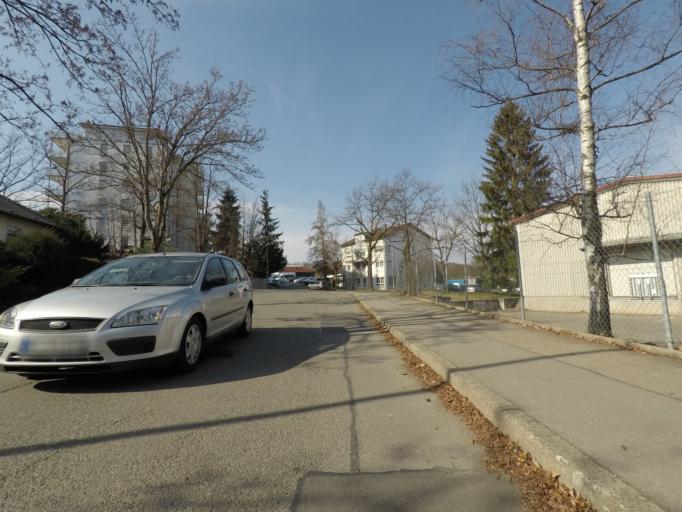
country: DE
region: Baden-Wuerttemberg
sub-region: Tuebingen Region
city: Metzingen
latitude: 48.5412
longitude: 9.2735
